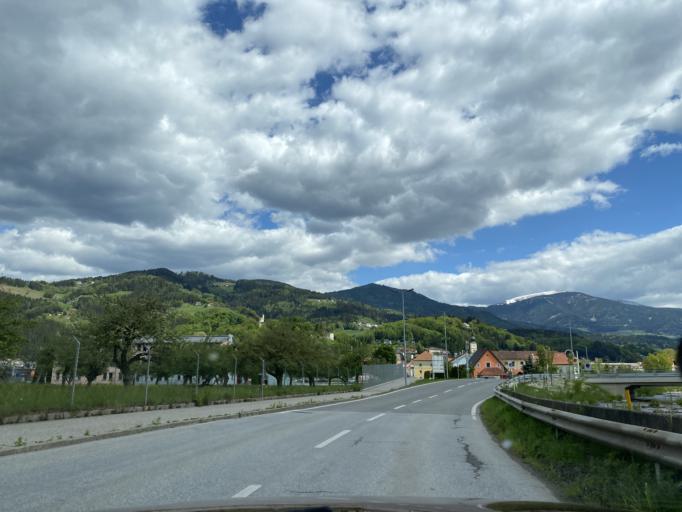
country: AT
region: Carinthia
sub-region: Politischer Bezirk Wolfsberg
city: Wolfsberg
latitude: 46.8412
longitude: 14.8353
